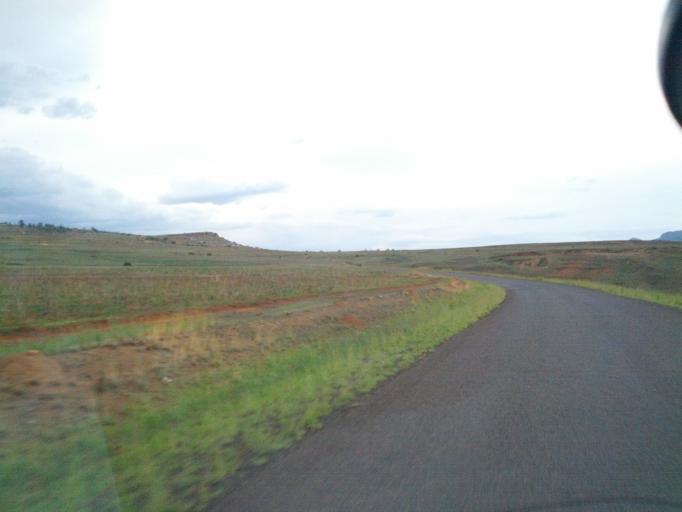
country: LS
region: Qacha's Nek
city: Qacha's Nek
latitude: -30.0553
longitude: 28.3821
